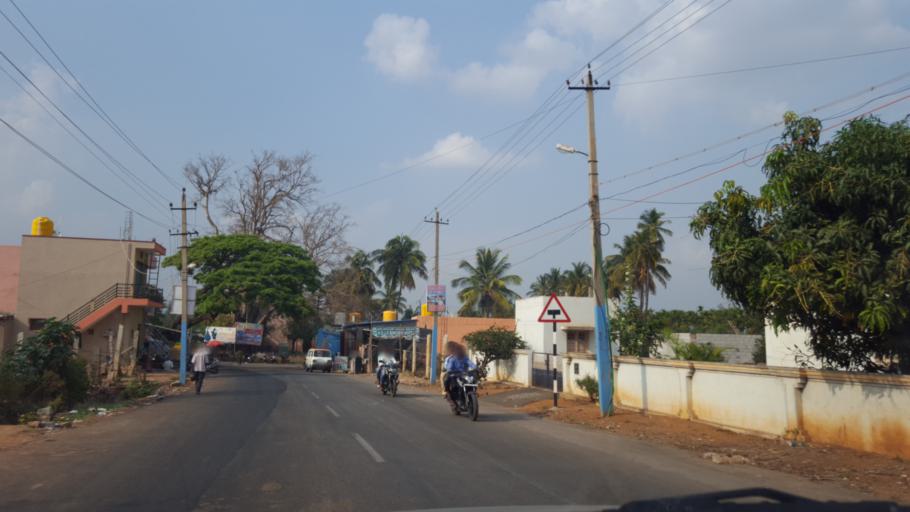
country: IN
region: Karnataka
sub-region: Chikkaballapur
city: Chik Ballapur
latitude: 13.3853
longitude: 77.7004
